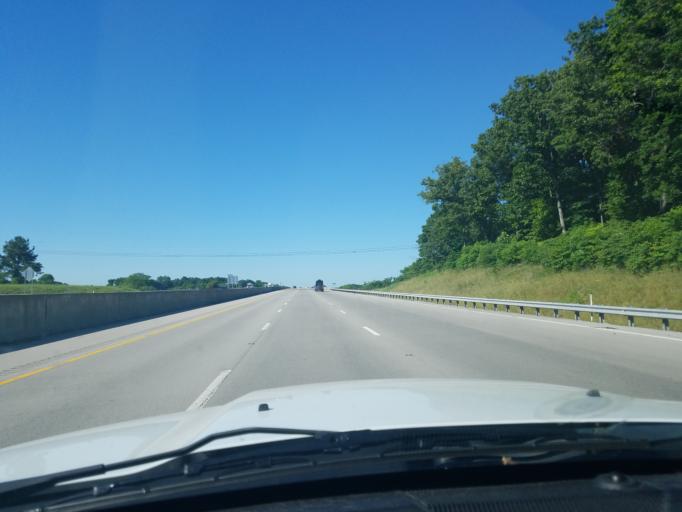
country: US
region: Kentucky
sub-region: Barren County
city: Cave City
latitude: 37.0925
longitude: -86.0593
